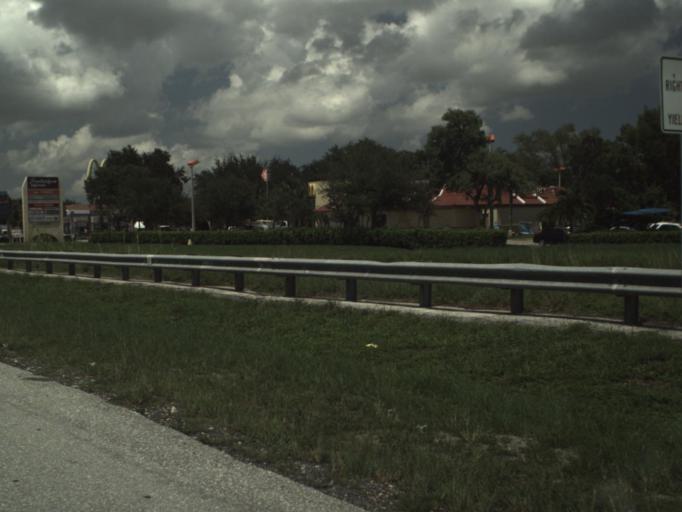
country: US
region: Florida
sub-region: Broward County
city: Parkland
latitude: 26.3319
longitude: -80.2029
